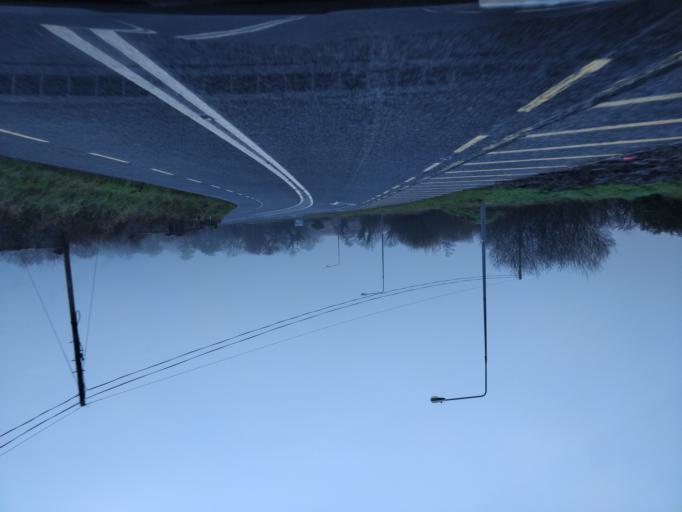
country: IE
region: Connaught
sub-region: Maigh Eo
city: Kiltamagh
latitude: 53.9046
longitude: -9.0668
